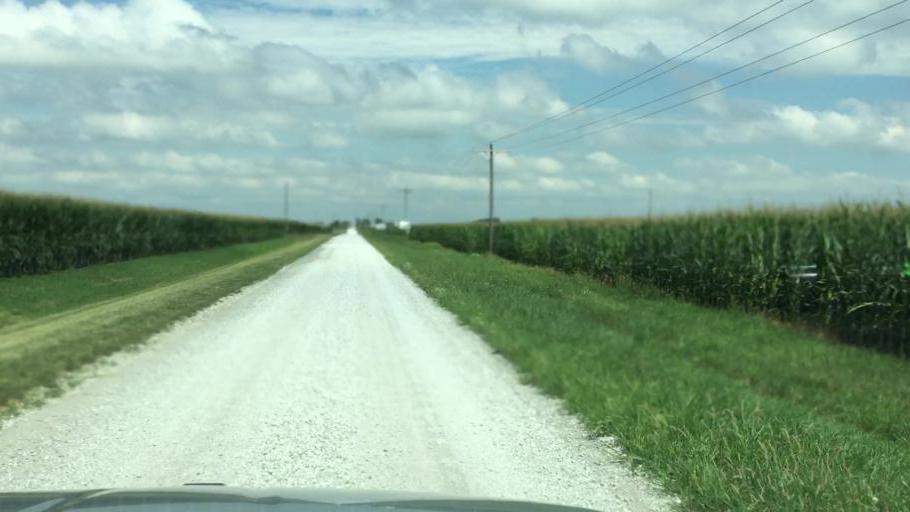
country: US
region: Illinois
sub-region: Hancock County
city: Nauvoo
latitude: 40.5216
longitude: -91.2903
